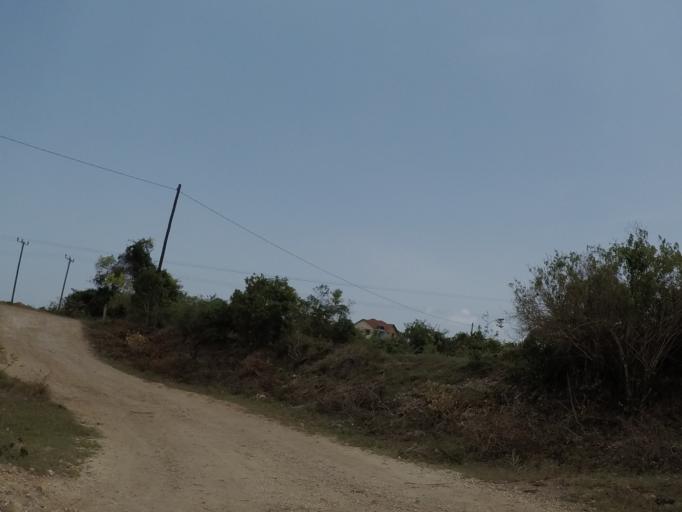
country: TZ
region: Zanzibar Central/South
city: Koani
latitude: -6.1938
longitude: 39.3086
